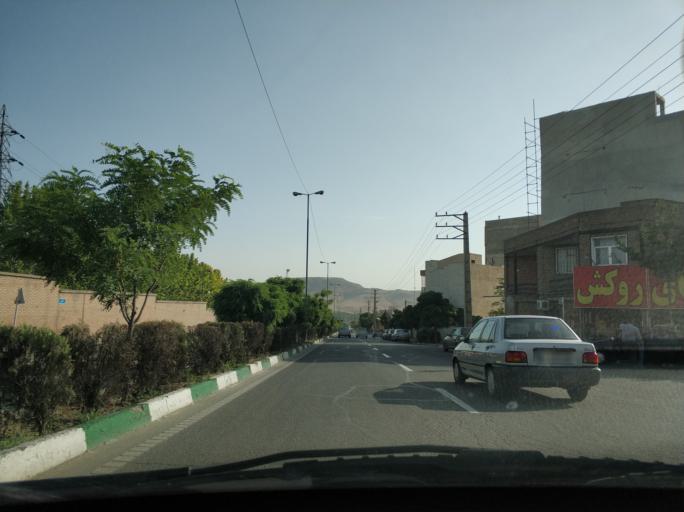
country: IR
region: Tehran
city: Tehran
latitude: 35.7316
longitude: 51.5949
